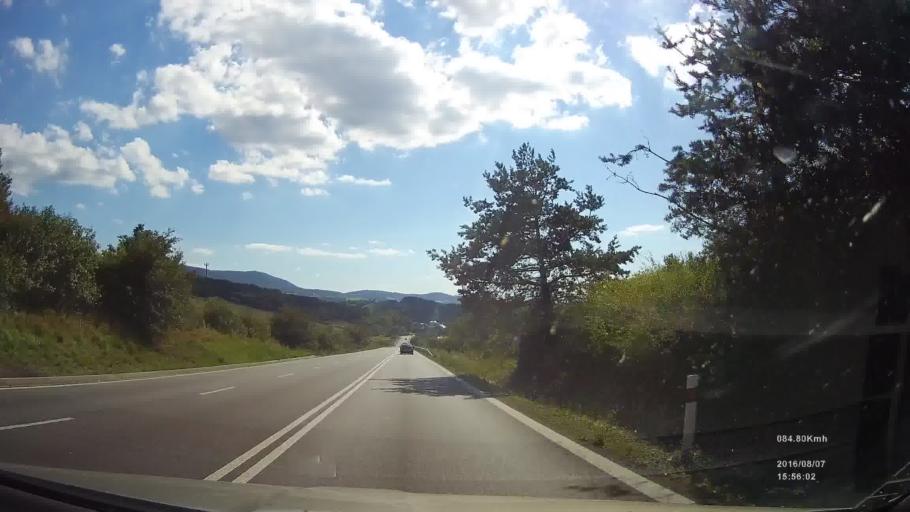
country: SK
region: Presovsky
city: Giraltovce
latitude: 49.0703
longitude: 21.4304
